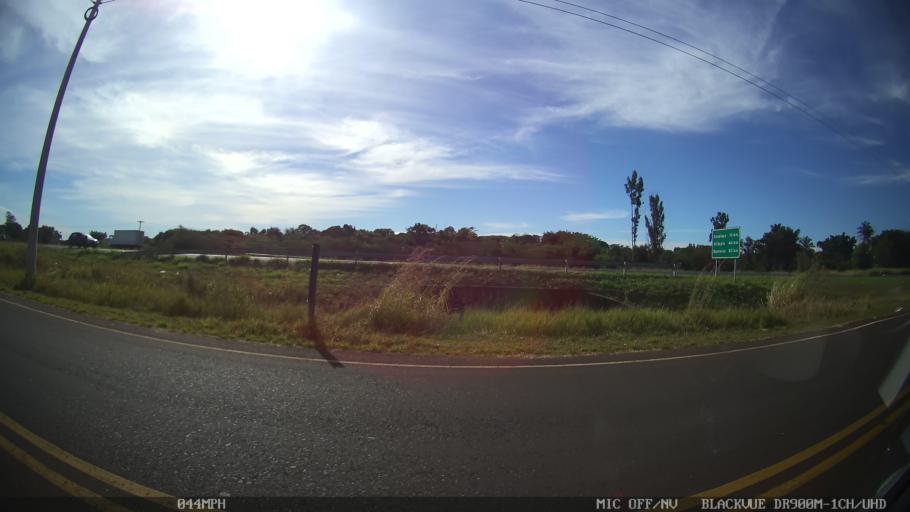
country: BR
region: Sao Paulo
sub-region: Sao Jose Do Rio Preto
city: Sao Jose do Rio Preto
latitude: -20.7964
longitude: -49.3189
